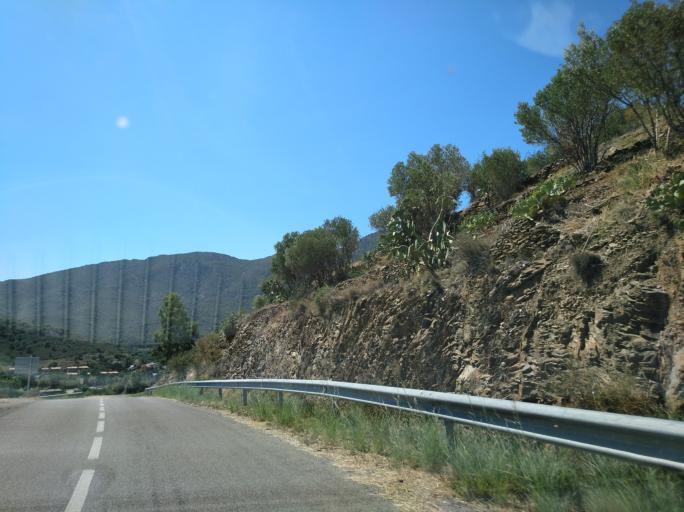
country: ES
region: Catalonia
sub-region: Provincia de Girona
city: Llanca
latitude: 42.3305
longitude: 3.1931
